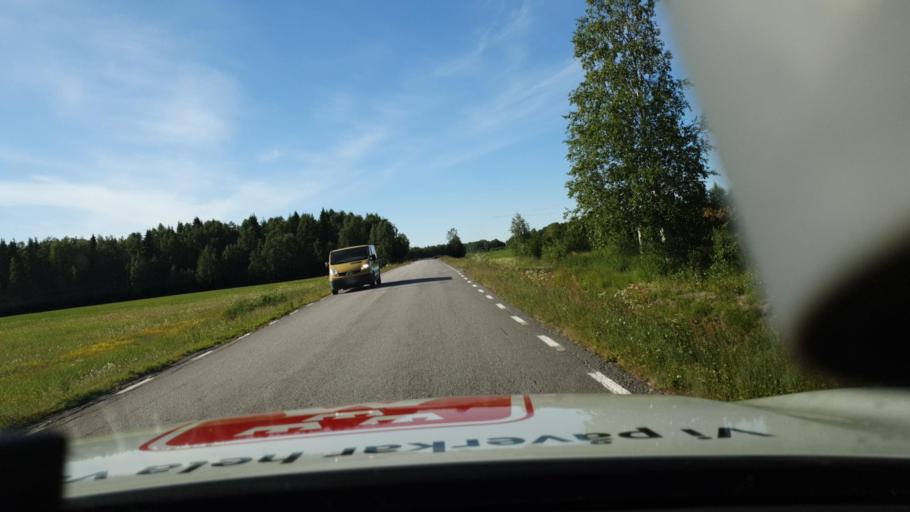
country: SE
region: Norrbotten
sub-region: Kalix Kommun
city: Toere
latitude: 65.8771
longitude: 22.6694
